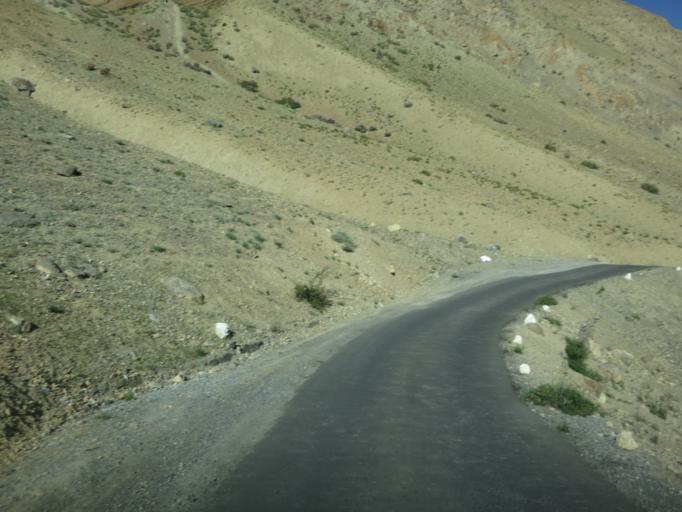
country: IN
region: Himachal Pradesh
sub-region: Shimla
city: Sarahan
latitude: 32.2620
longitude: 78.0384
